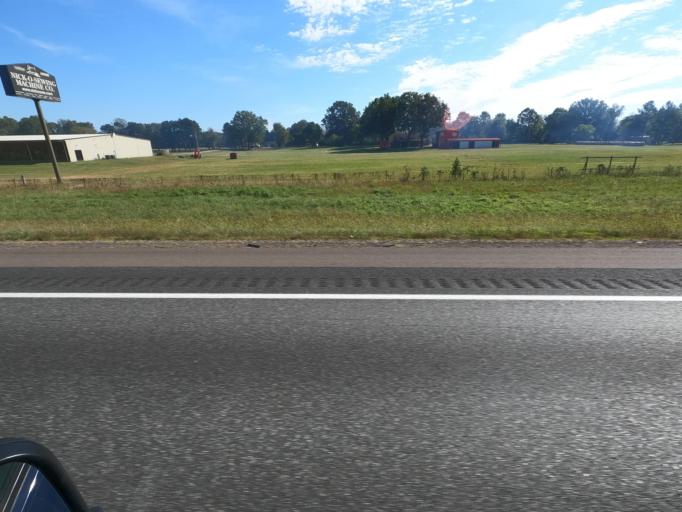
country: US
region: Tennessee
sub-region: Haywood County
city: Brownsville
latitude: 35.4852
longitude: -89.2721
